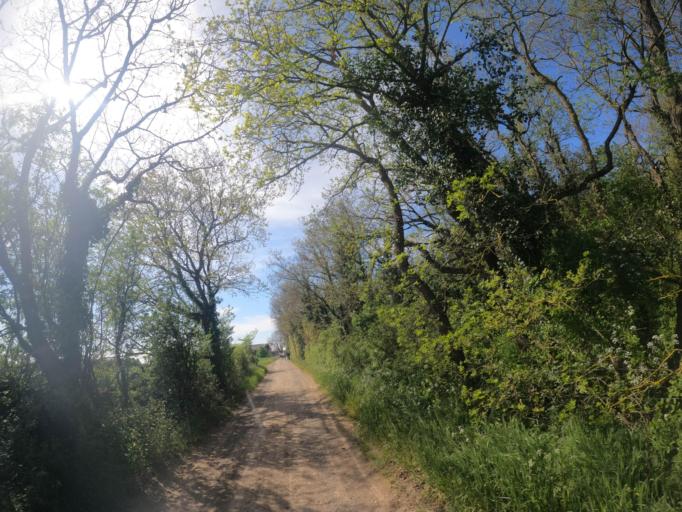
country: FR
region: Poitou-Charentes
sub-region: Departement des Deux-Sevres
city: Saint-Varent
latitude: 46.9142
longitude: -0.2126
